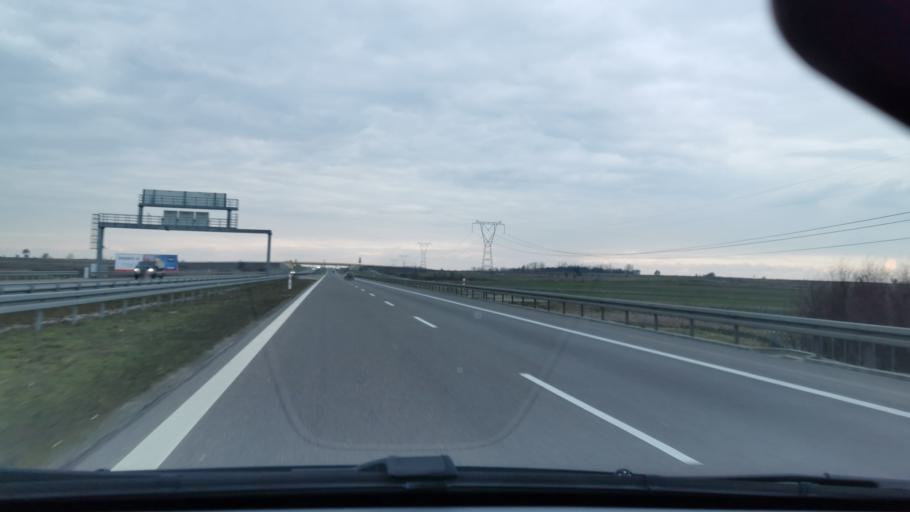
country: PL
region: Lublin Voivodeship
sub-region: Powiat pulawski
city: Markuszow
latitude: 51.3847
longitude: 22.2710
